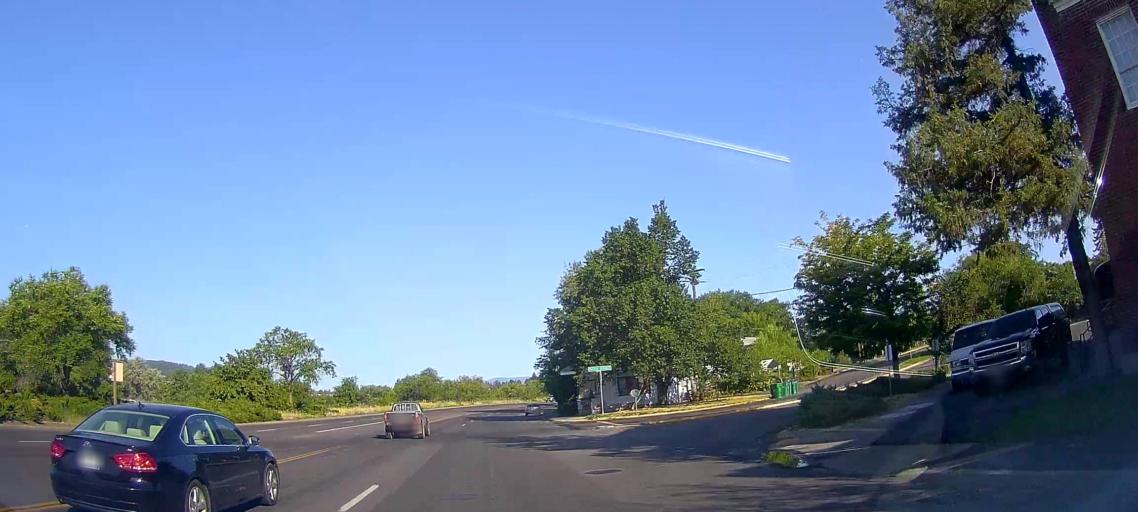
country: US
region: Oregon
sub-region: Klamath County
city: Klamath Falls
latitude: 42.2298
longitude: -121.7688
